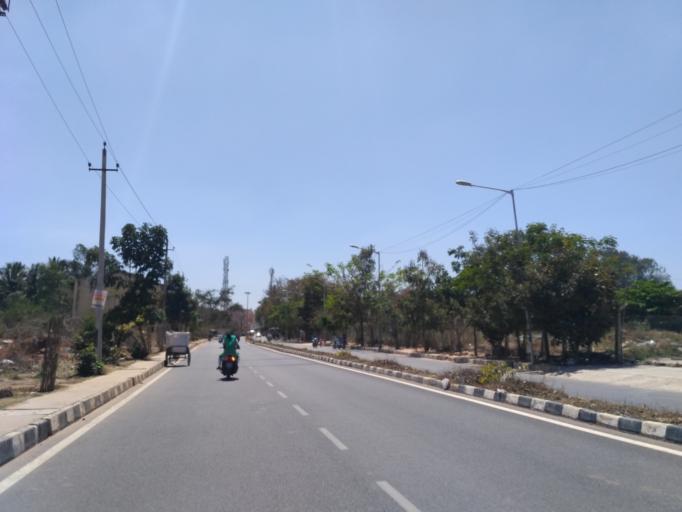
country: IN
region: Karnataka
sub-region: Bangalore Urban
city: Yelahanka
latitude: 13.0902
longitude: 77.5897
